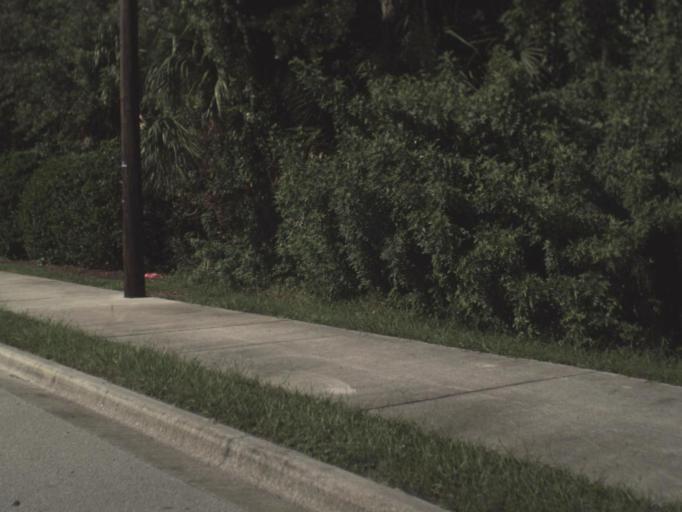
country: US
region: Florida
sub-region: Sarasota County
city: Englewood
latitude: 26.9809
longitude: -82.3596
